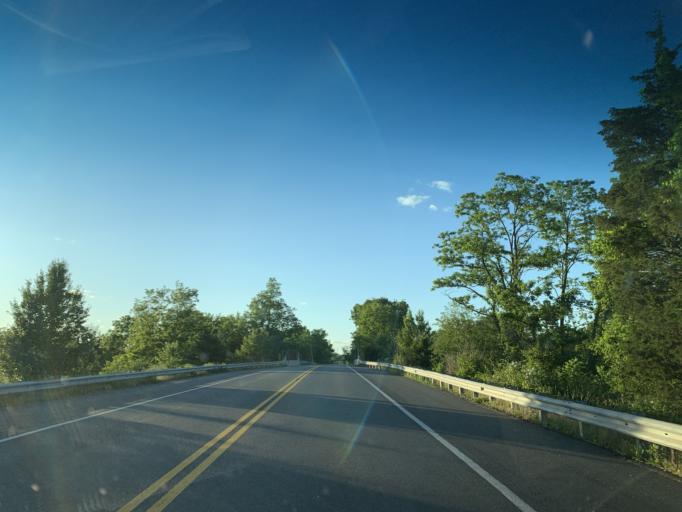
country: US
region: Maryland
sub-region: Cecil County
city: Elkton
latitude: 39.6474
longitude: -75.8480
